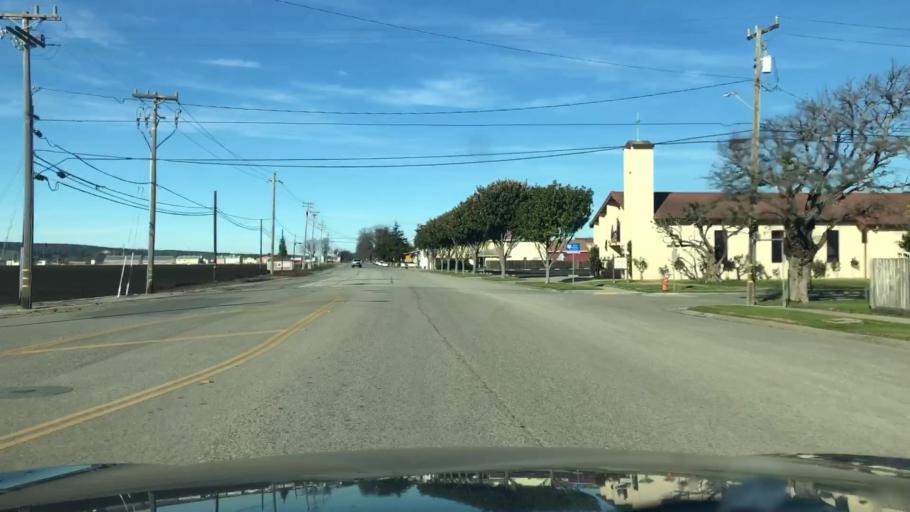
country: US
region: California
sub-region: Monterey County
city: Salinas
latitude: 36.6216
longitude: -121.6451
